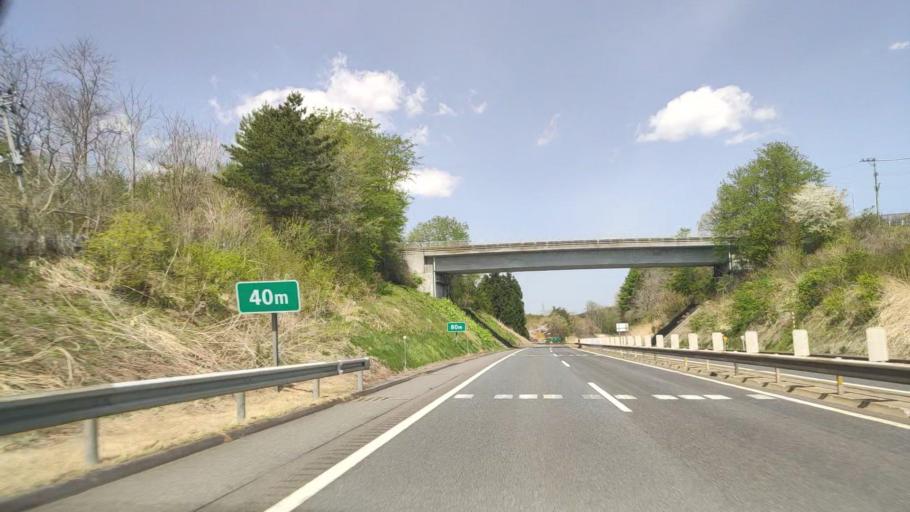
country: JP
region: Aomori
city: Hachinohe
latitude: 40.4162
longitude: 141.4415
